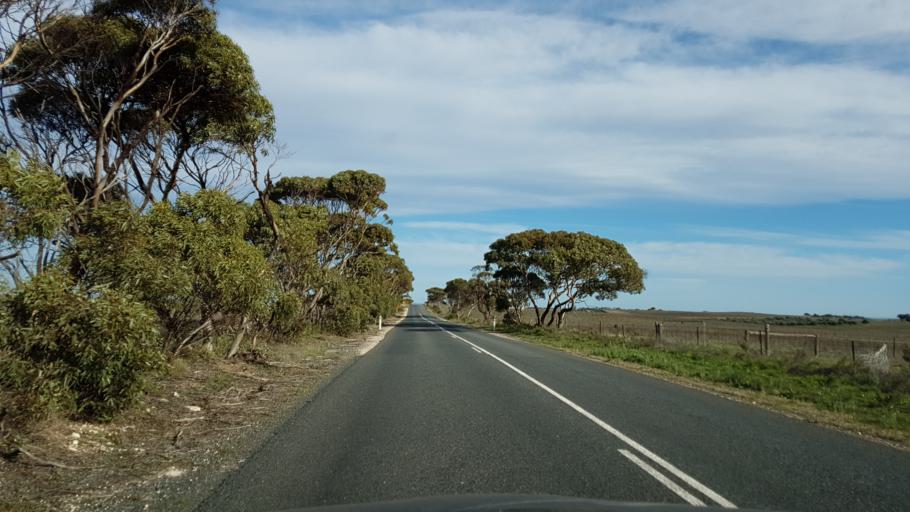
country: AU
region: South Australia
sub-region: Murray Bridge
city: Tailem Bend
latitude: -35.1832
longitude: 139.4592
